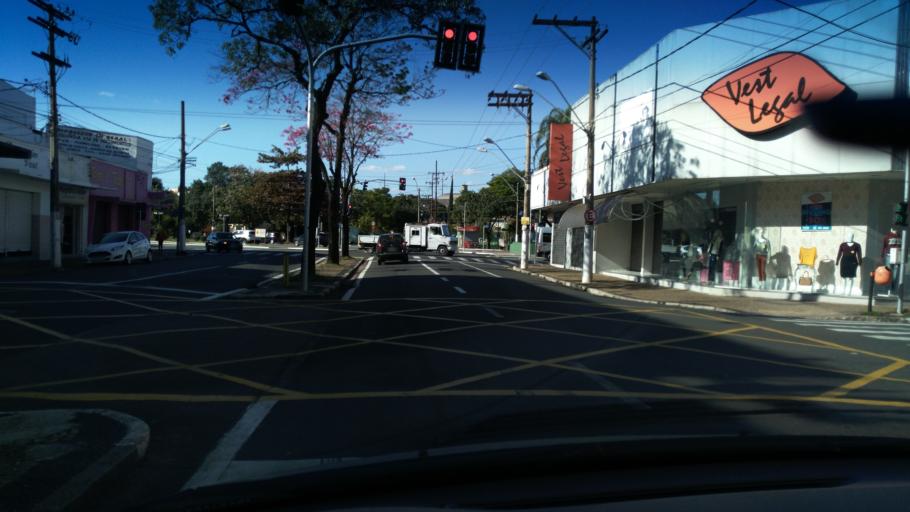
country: BR
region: Sao Paulo
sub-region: Valinhos
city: Valinhos
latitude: -22.9685
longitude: -46.9950
